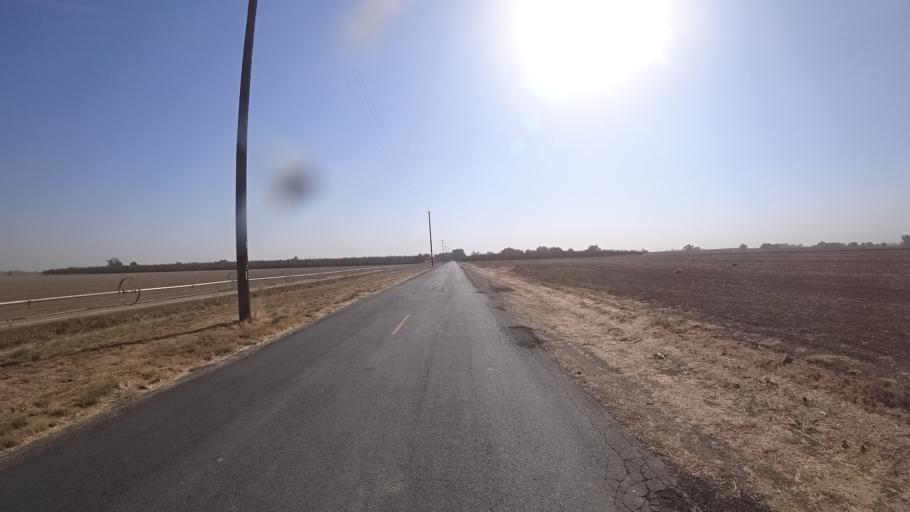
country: US
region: California
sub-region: Yolo County
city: Woodland
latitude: 38.7122
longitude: -121.8567
